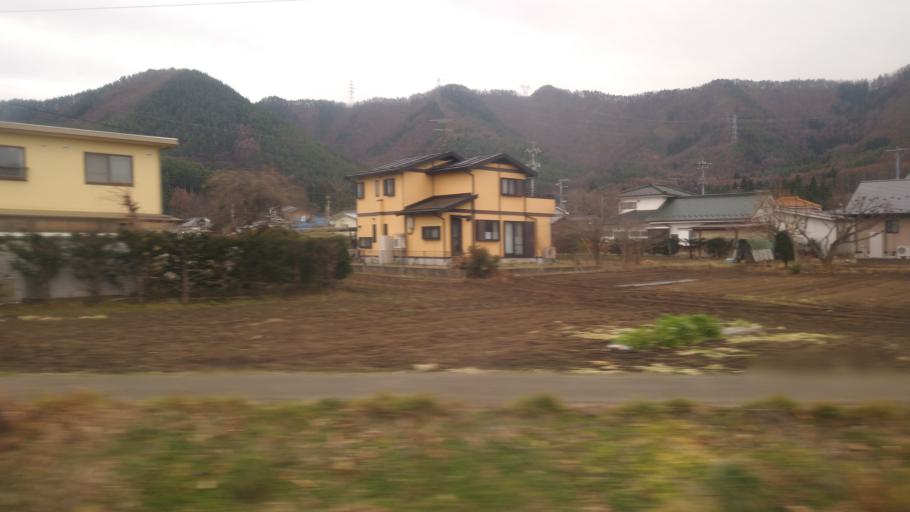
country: JP
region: Nagano
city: Shiojiri
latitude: 36.0980
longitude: 137.9294
